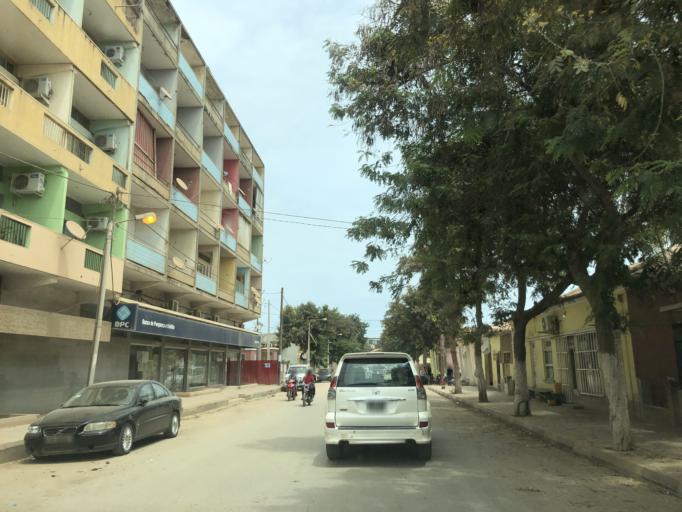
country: AO
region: Cuanza Sul
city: Sumbe
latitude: -11.2004
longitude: 13.8419
